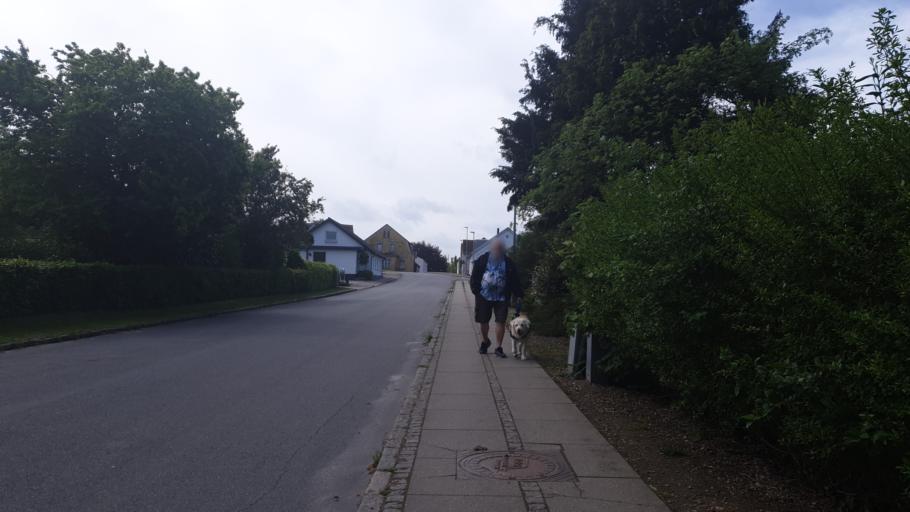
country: DK
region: Central Jutland
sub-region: Hedensted Kommune
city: Hedensted
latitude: 55.8055
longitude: 9.7018
